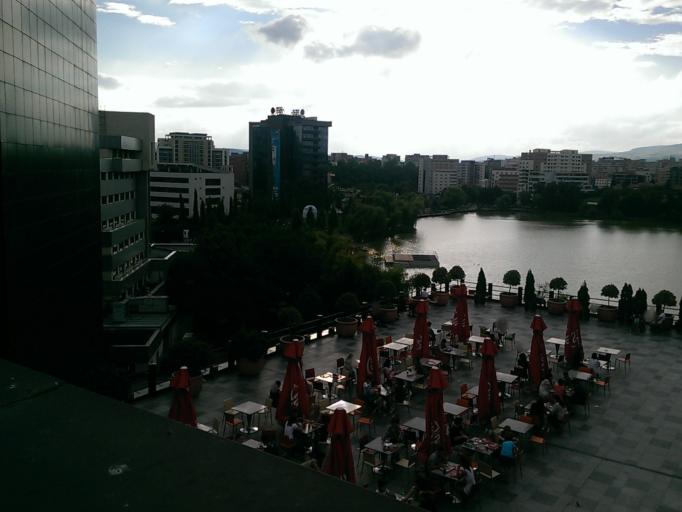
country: RO
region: Cluj
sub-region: Municipiul Cluj-Napoca
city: Cluj-Napoca
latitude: 46.7728
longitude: 23.6282
